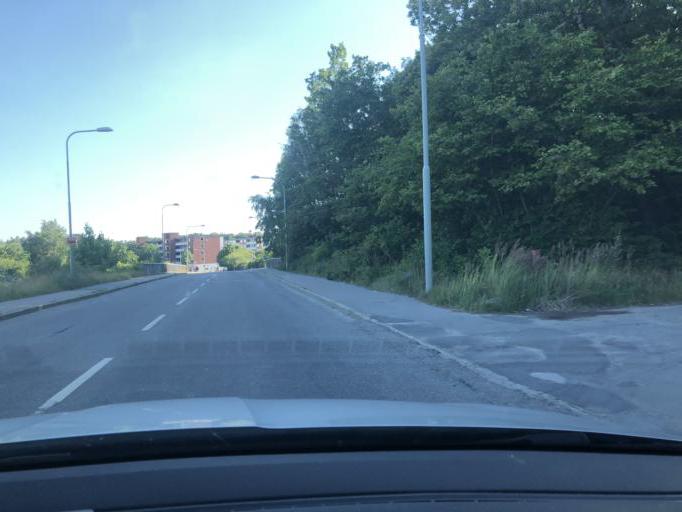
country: SE
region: Stockholm
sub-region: Botkyrka Kommun
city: Fittja
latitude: 59.2709
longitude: 17.8888
